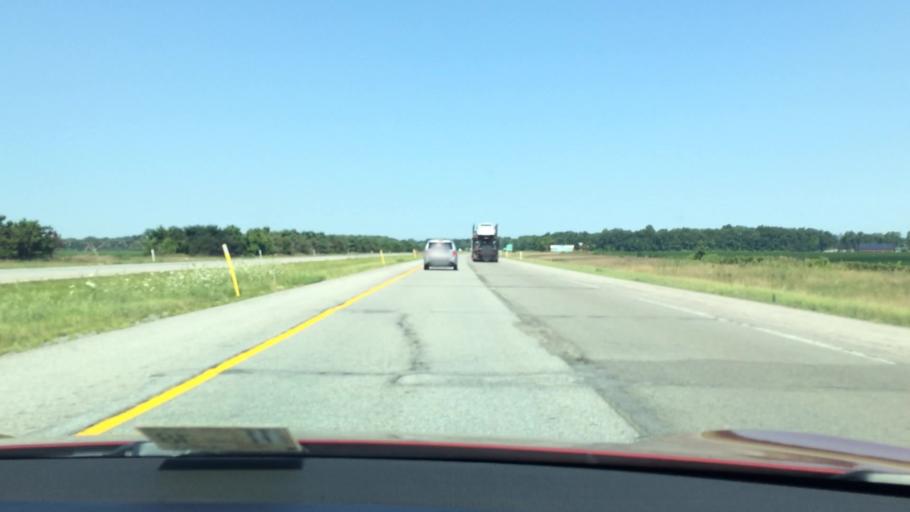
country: US
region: Michigan
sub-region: Saint Joseph County
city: White Pigeon
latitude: 41.7522
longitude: -85.6303
